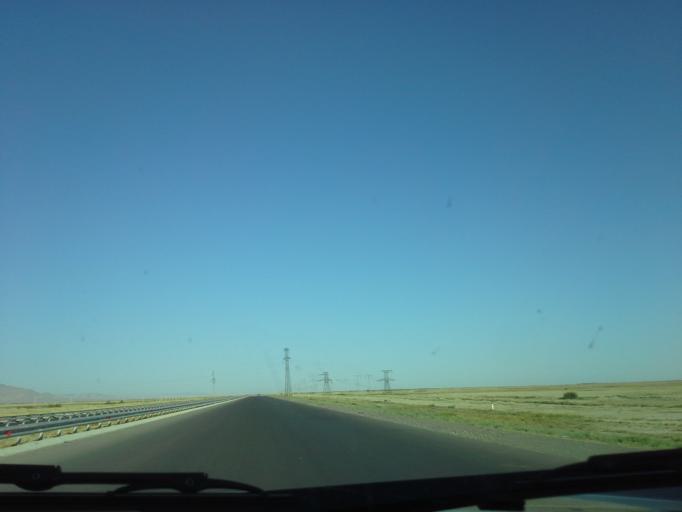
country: TM
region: Balkan
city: Serdar
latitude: 39.0197
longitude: 56.2117
